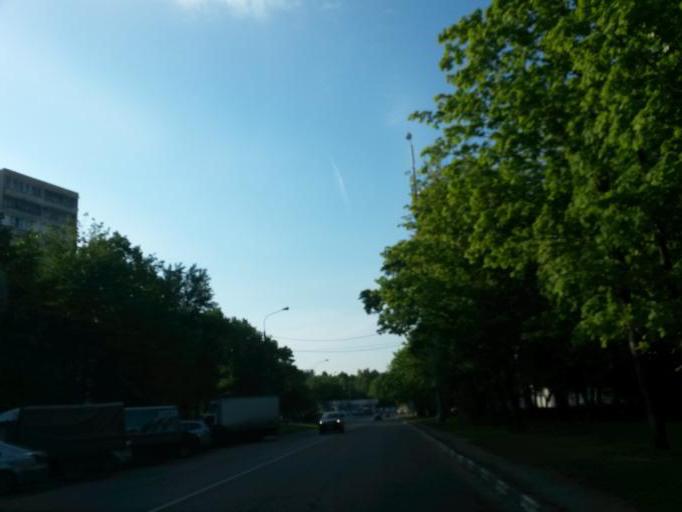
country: RU
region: Moskovskaya
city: Biryulevo Zapadnoye
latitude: 55.5908
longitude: 37.6546
